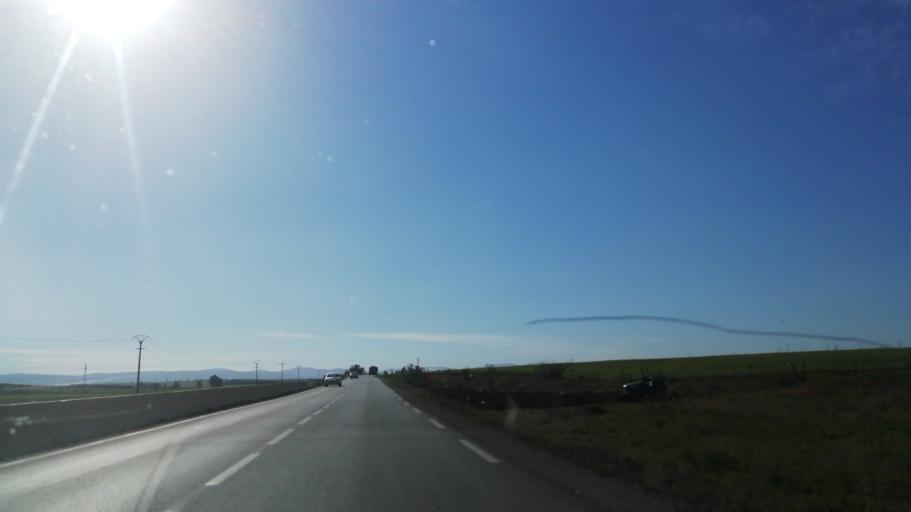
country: DZ
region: Tlemcen
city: Ouled Mimoun
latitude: 35.0011
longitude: -0.9073
